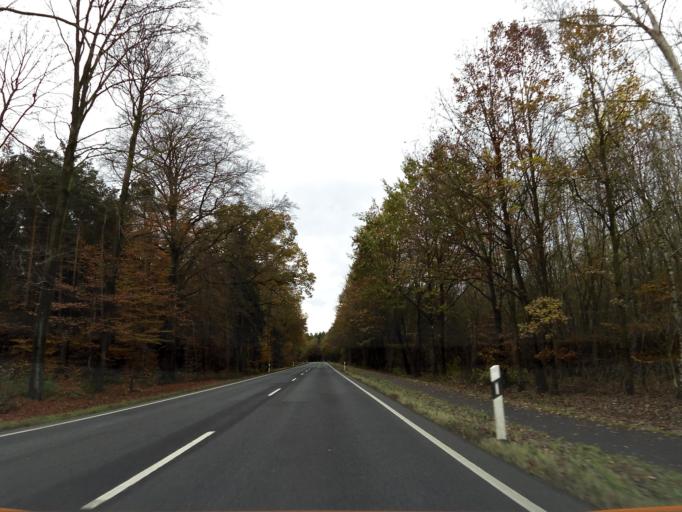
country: DE
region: Lower Saxony
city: Uelzen
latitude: 52.9524
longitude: 10.5117
